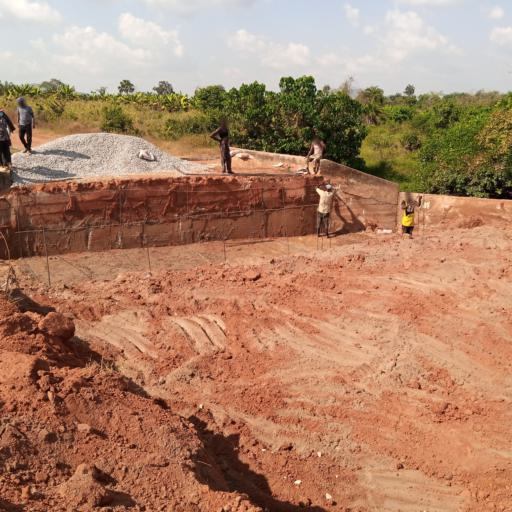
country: NG
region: Osun
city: Iwo
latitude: 7.7118
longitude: 4.1112
